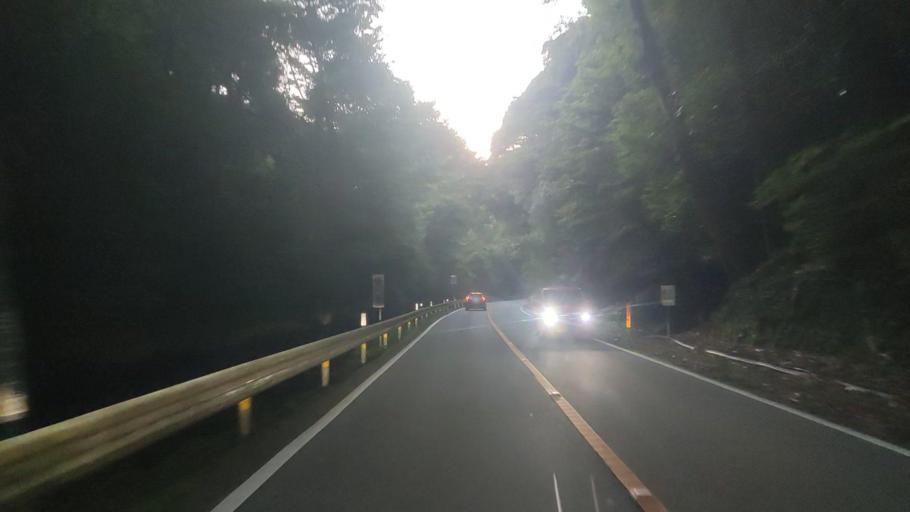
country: JP
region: Mie
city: Ise
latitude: 34.4167
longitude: 136.7622
